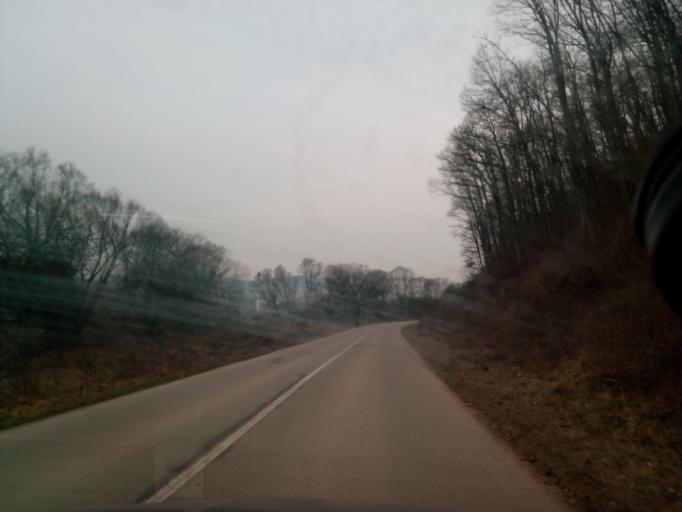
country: SK
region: Kosicky
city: Medzev
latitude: 48.6960
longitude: 20.9179
